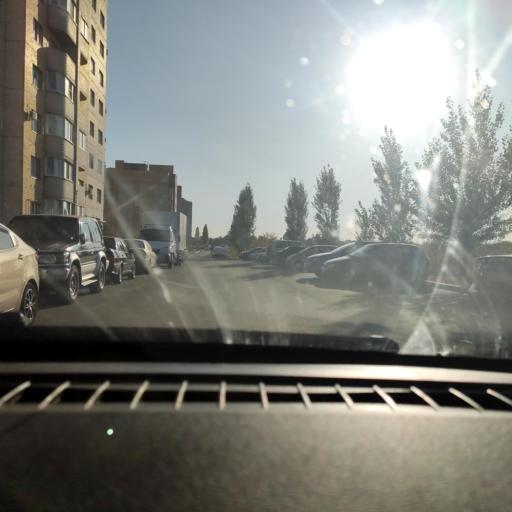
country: RU
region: Voronezj
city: Somovo
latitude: 51.6761
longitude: 39.2901
